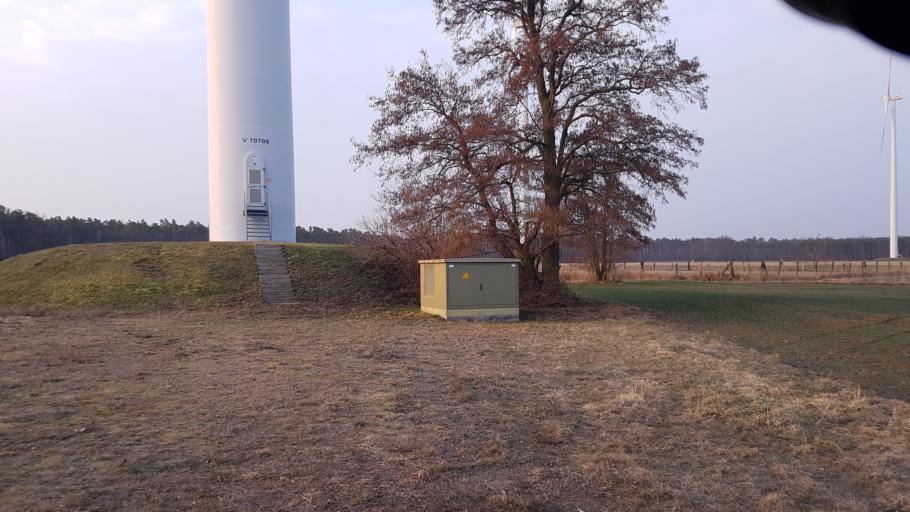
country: DE
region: Brandenburg
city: Falkenberg
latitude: 51.5689
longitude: 13.3045
